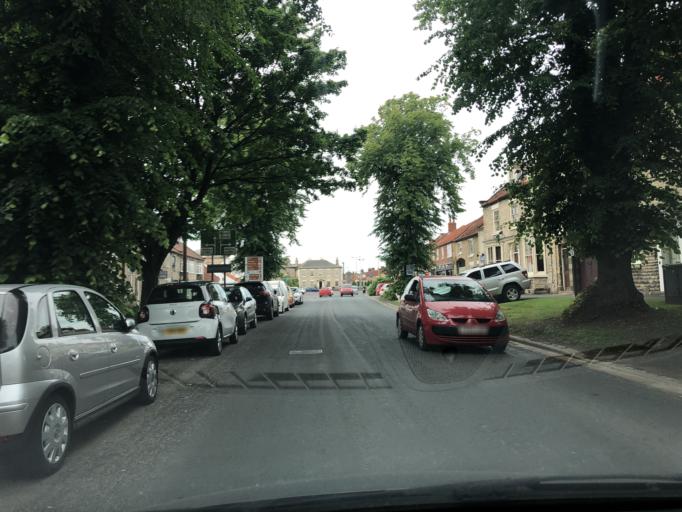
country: GB
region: England
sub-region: North Yorkshire
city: Pickering
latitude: 54.2430
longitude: -0.7731
